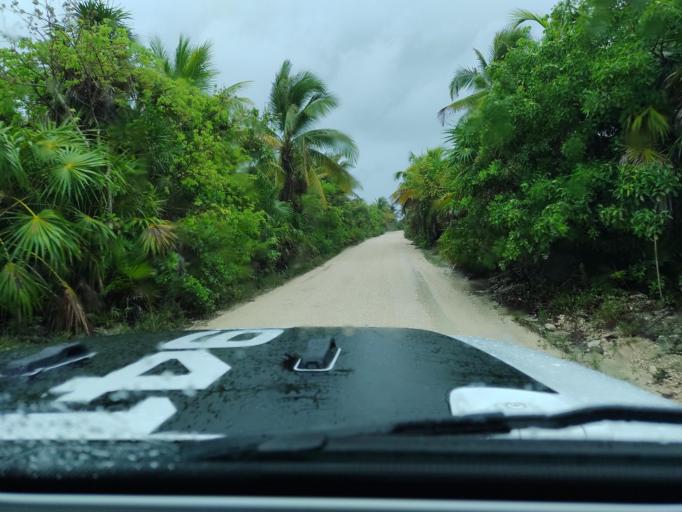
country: MX
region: Quintana Roo
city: Tulum
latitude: 19.9872
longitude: -87.4648
